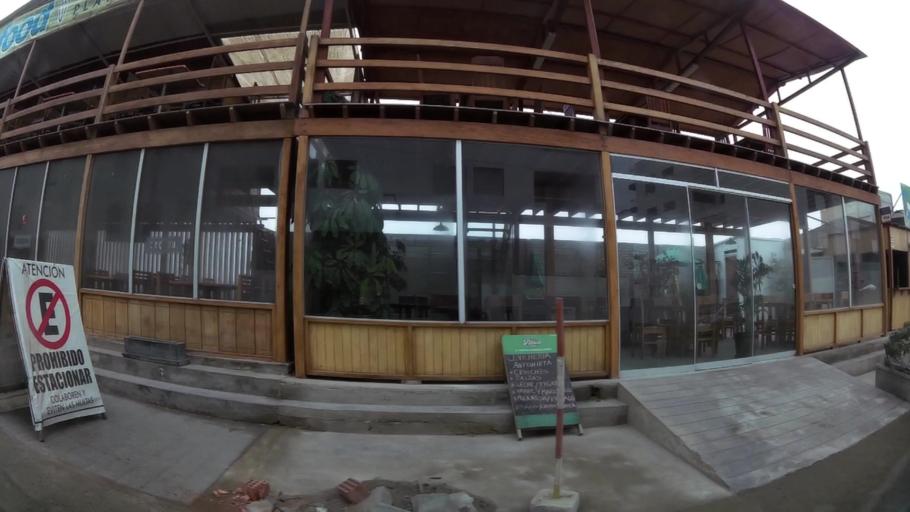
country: PE
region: Lima
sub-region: Lima
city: Punta Hermosa
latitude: -12.3242
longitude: -76.8344
